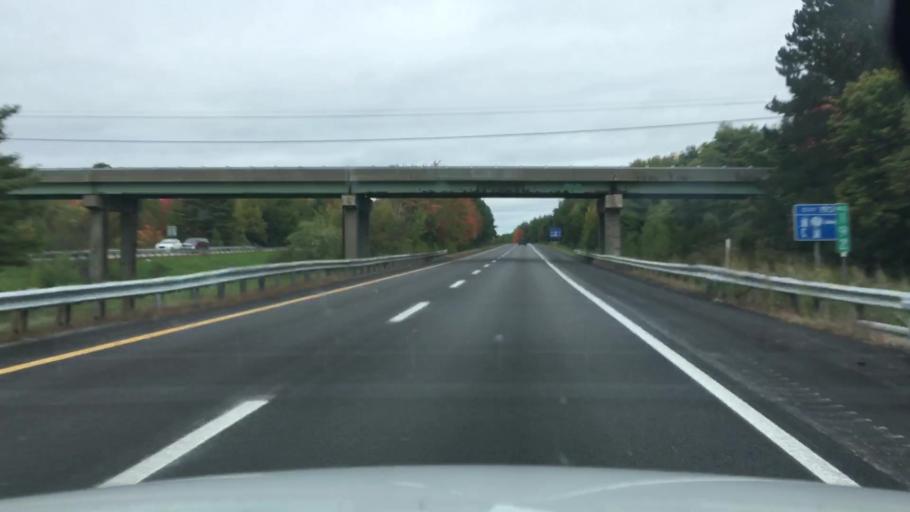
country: US
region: Maine
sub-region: Penobscot County
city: Orono
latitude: 44.8891
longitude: -68.6935
